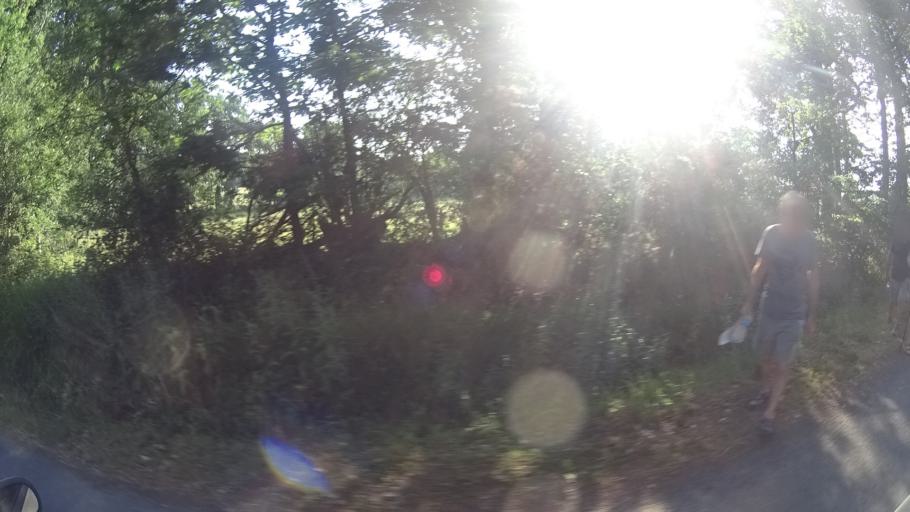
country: FR
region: Brittany
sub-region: Departement d'Ille-et-Vilaine
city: Bains-sur-Oust
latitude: 47.6771
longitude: -2.0697
